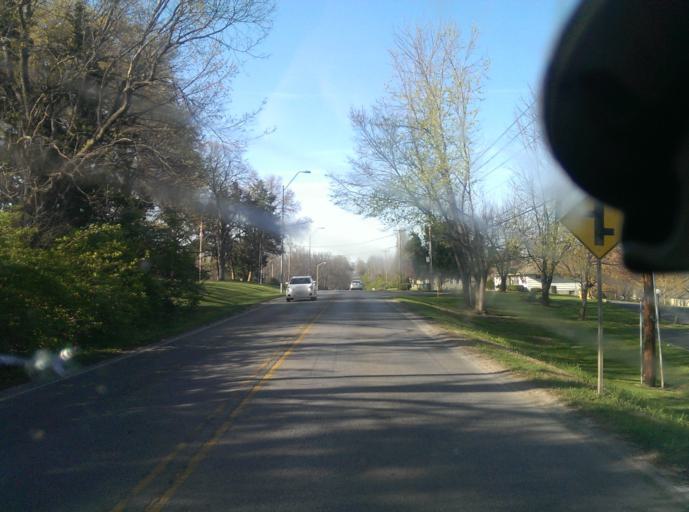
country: US
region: Missouri
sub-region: Jackson County
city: Grandview
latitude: 38.9040
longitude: -94.5850
